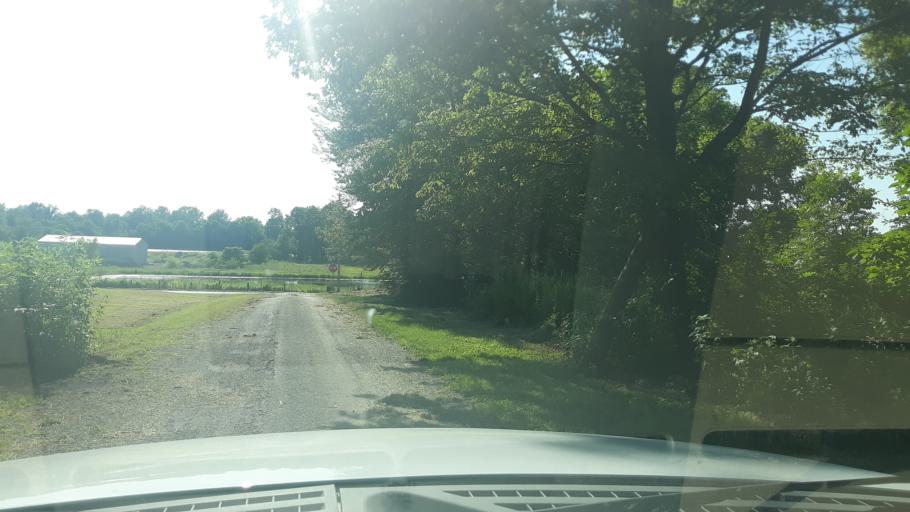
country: US
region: Illinois
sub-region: Saline County
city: Harrisburg
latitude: 37.8441
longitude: -88.6136
